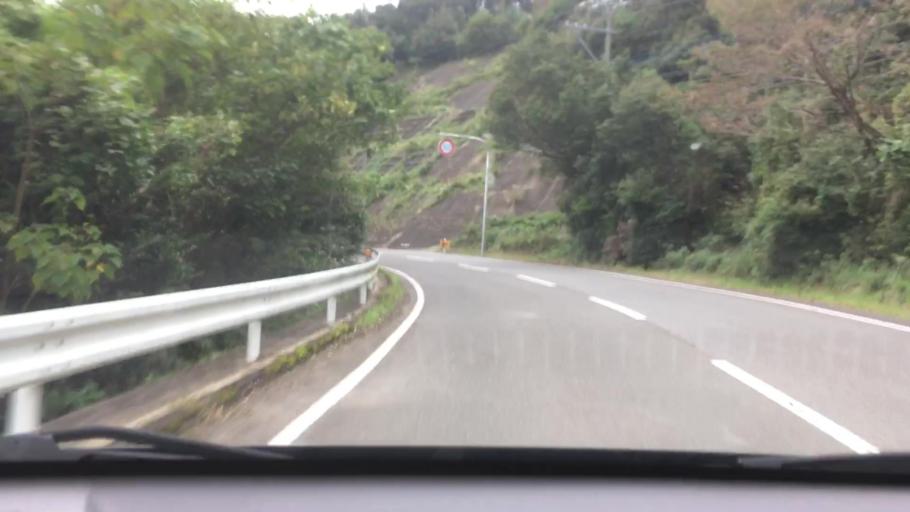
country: JP
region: Nagasaki
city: Sasebo
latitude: 32.9767
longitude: 129.7079
